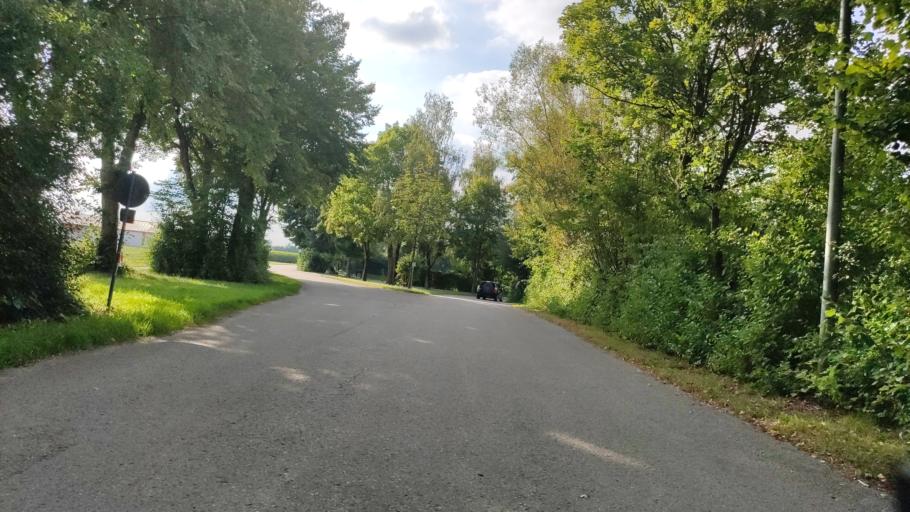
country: DE
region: Bavaria
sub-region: Upper Bavaria
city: Prittriching
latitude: 48.2077
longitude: 10.9221
